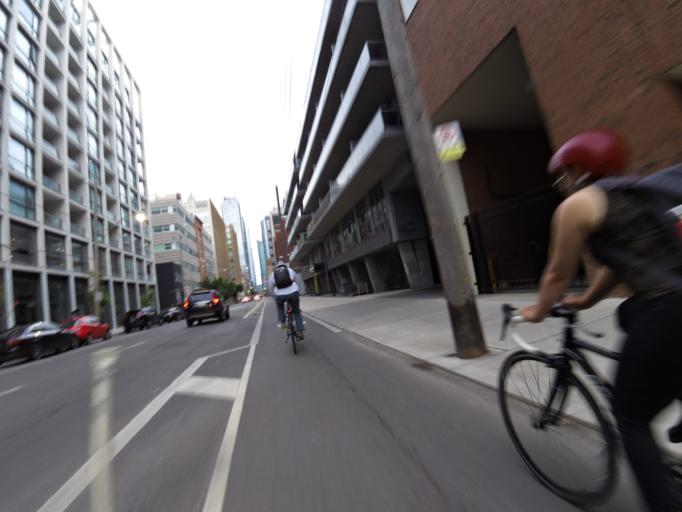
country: CA
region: Ontario
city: Toronto
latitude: 43.6463
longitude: -79.3979
